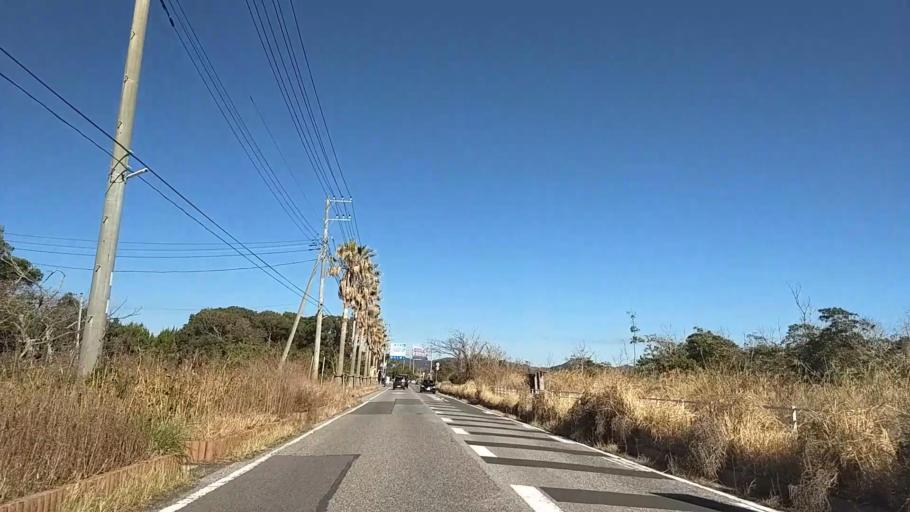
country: JP
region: Chiba
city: Tateyama
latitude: 35.0072
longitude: 139.9764
